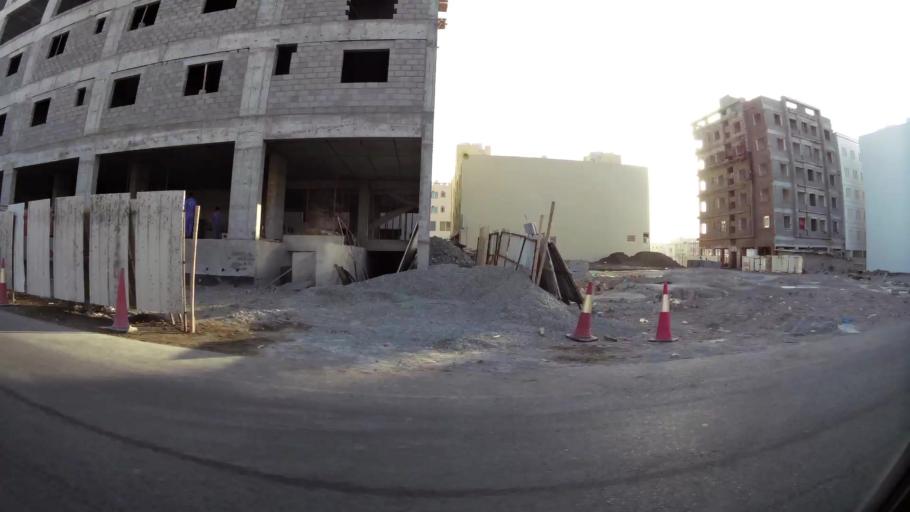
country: OM
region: Muhafazat Masqat
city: As Sib al Jadidah
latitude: 23.5929
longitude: 58.1439
